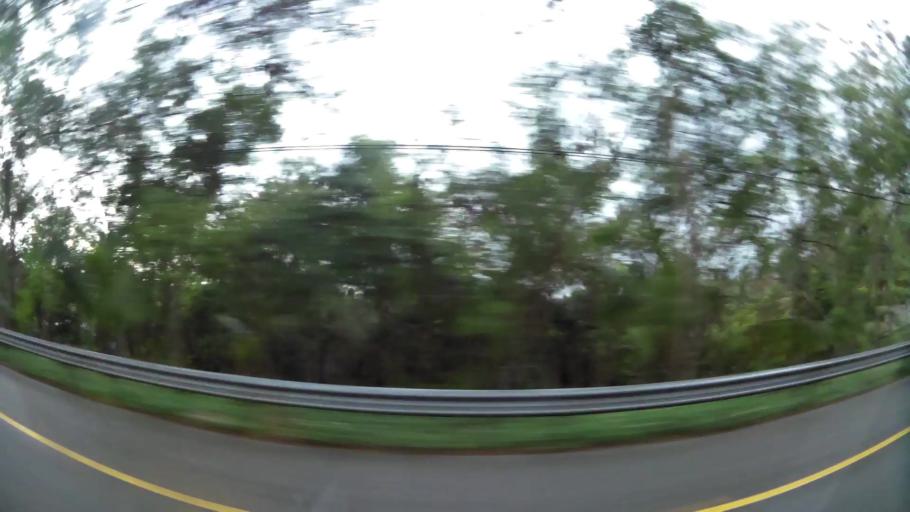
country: DO
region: San Cristobal
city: Villa Altagracia
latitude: 18.5984
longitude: -70.1329
